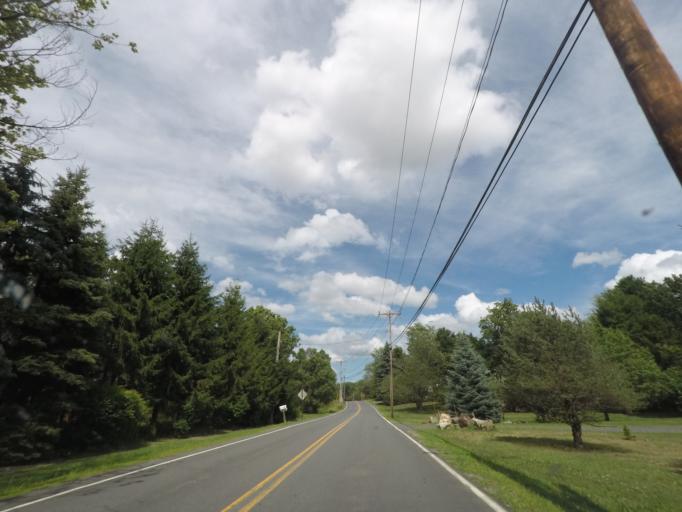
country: US
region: New York
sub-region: Rensselaer County
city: Wynantskill
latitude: 42.7255
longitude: -73.6191
